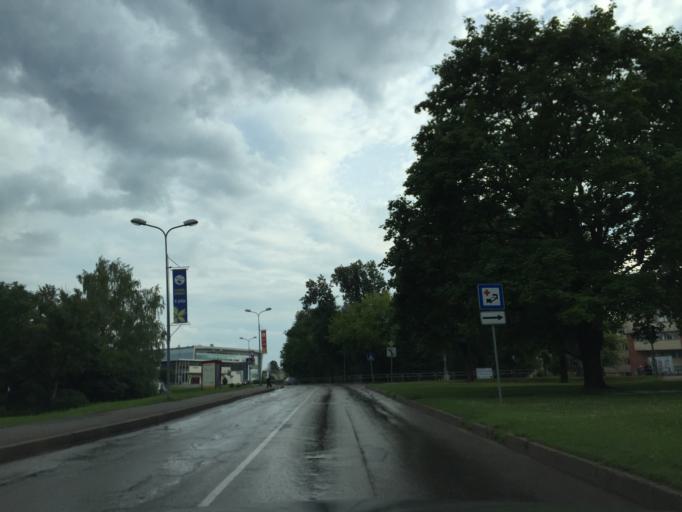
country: LV
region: Dobeles Rajons
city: Dobele
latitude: 56.6229
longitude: 23.2717
